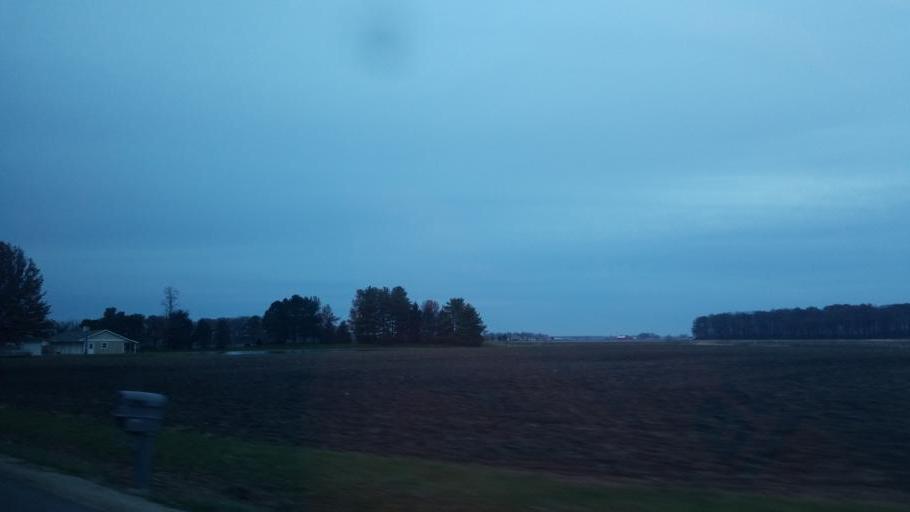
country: US
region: Indiana
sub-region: Adams County
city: Berne
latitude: 40.7372
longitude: -84.9947
